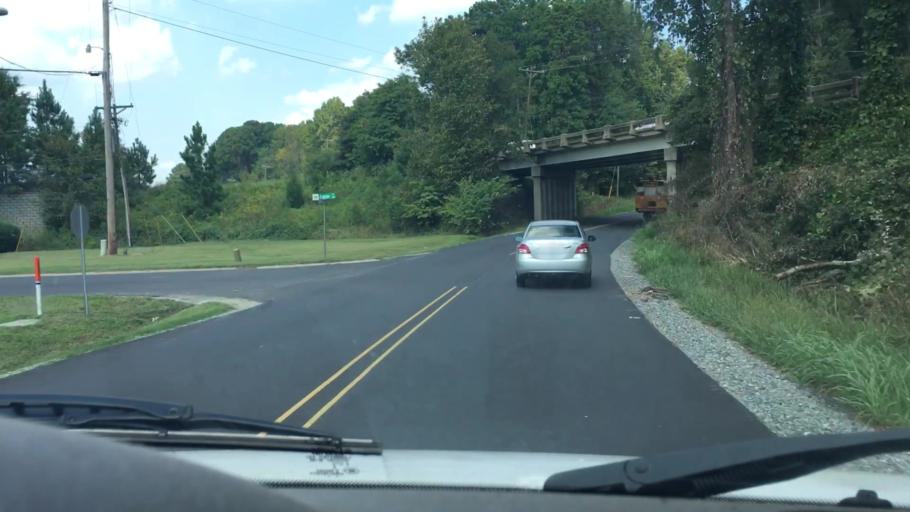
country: US
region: North Carolina
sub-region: Mecklenburg County
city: Huntersville
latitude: 35.3978
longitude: -80.8515
